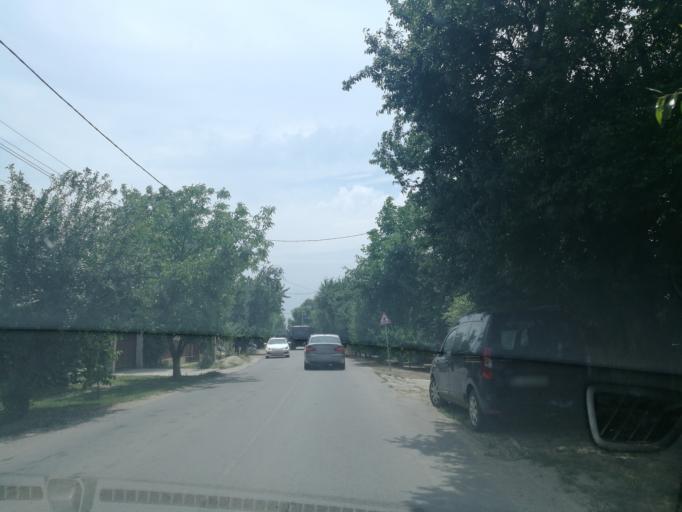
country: RO
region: Ilfov
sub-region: Comuna Vidra
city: Cretesti
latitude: 44.2805
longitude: 26.1338
